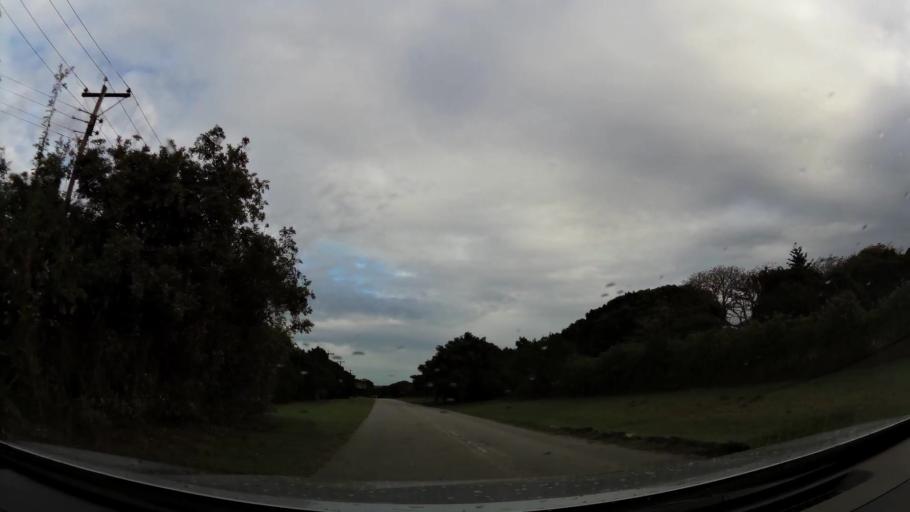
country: ZA
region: Eastern Cape
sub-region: Nelson Mandela Bay Metropolitan Municipality
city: Port Elizabeth
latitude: -34.0167
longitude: 25.5018
